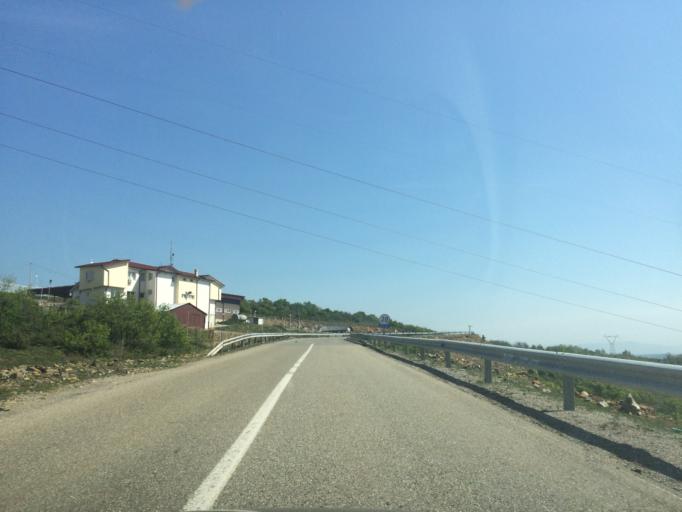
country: XK
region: Gjakova
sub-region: Komuna e Junikut
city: Junik
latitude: 42.4117
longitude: 20.2219
